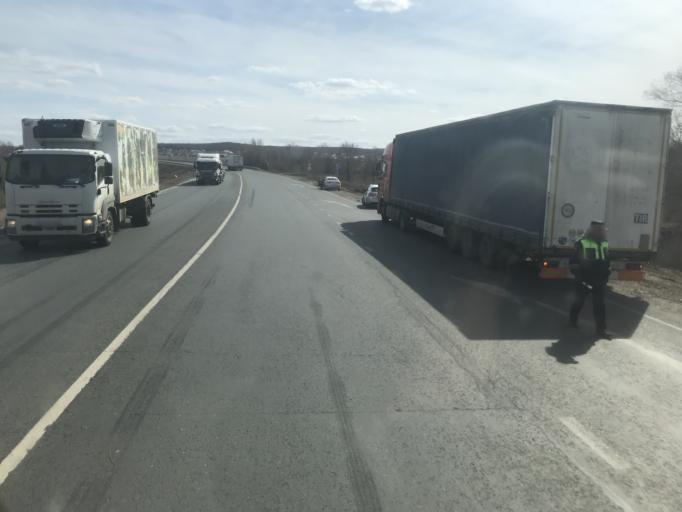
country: RU
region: Samara
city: Novosemeykino
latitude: 53.4113
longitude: 50.3501
